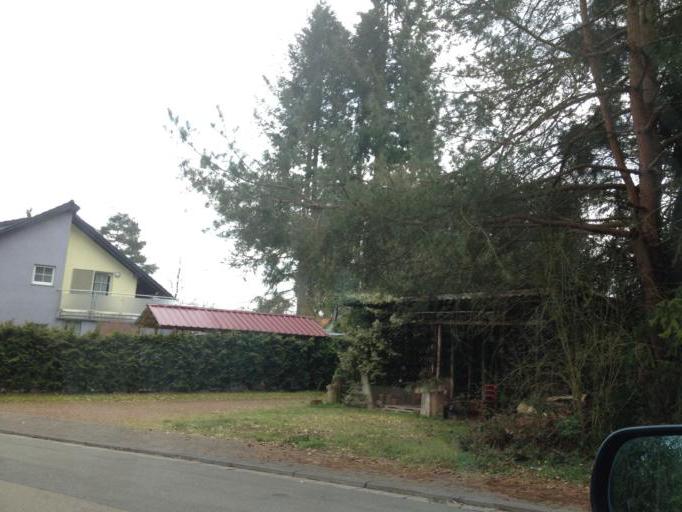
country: DE
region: Saarland
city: Bexbach
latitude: 49.3322
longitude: 7.2273
